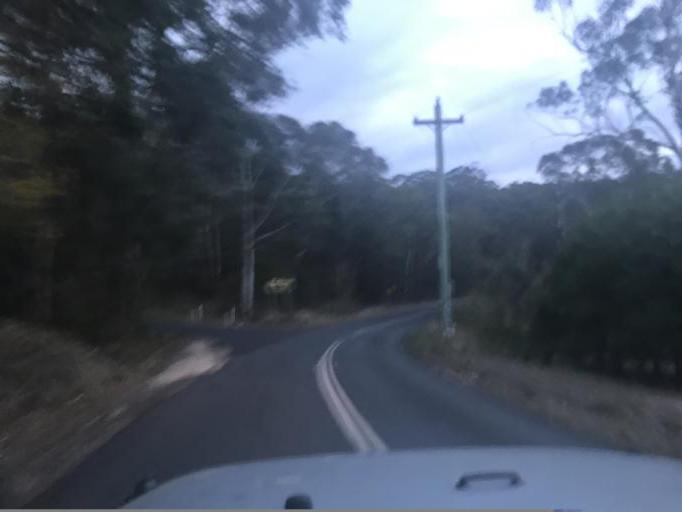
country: AU
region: New South Wales
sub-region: Hawkesbury
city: Pitt Town
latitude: -33.5039
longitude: 150.8636
